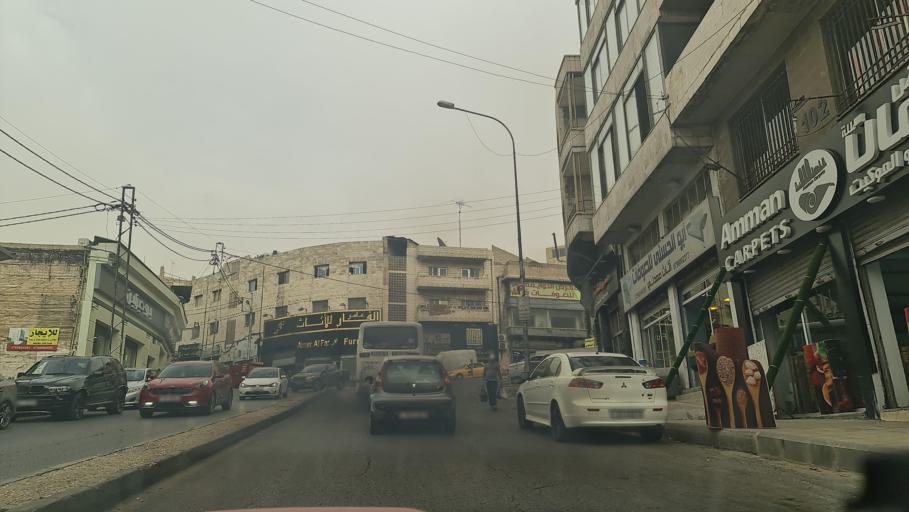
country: JO
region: Amman
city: Amman
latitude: 31.9374
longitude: 35.9304
